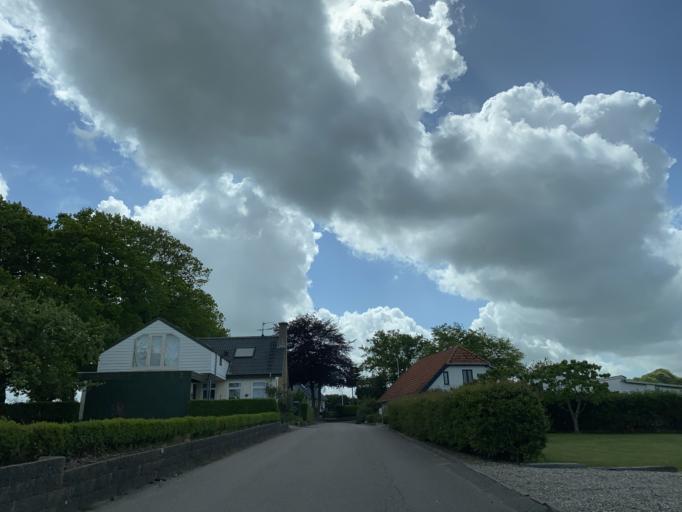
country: DK
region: South Denmark
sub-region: Aabenraa Kommune
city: Lojt Kirkeby
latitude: 55.0138
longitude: 9.4934
